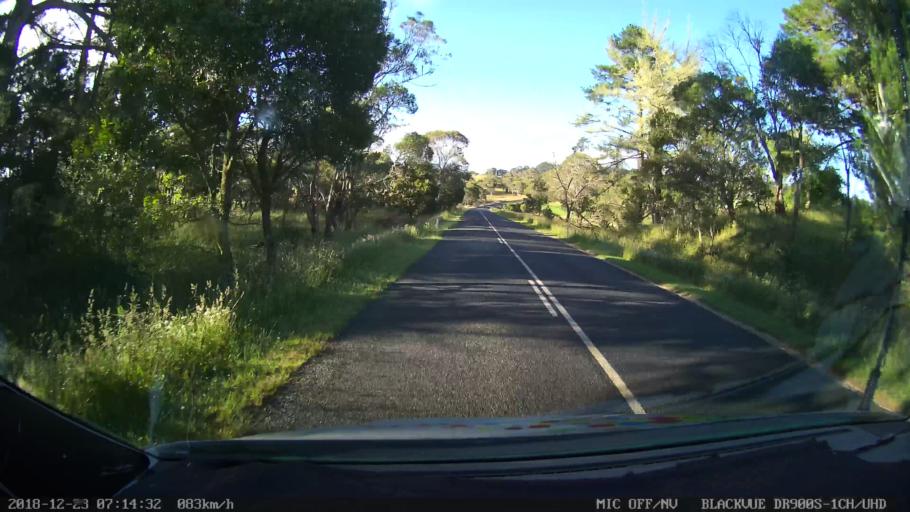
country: AU
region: New South Wales
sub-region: Bellingen
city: Dorrigo
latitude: -30.4363
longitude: 152.3219
